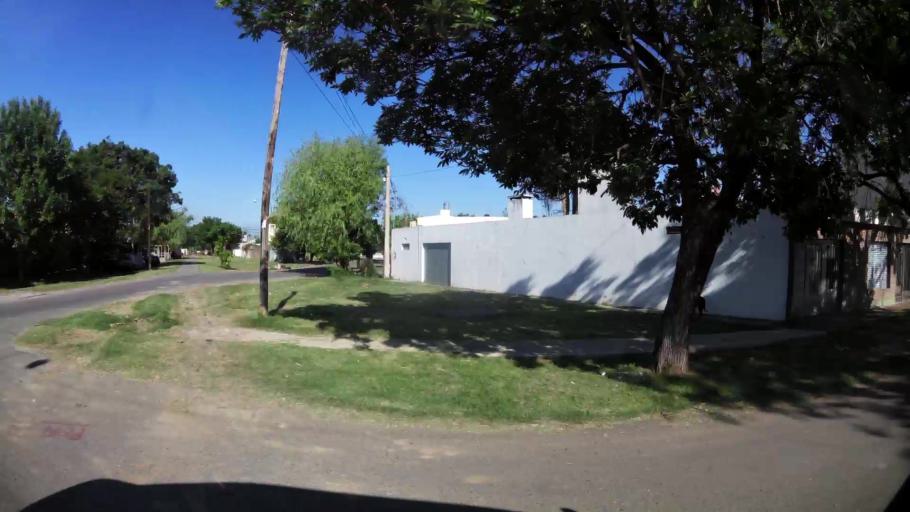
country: AR
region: Santa Fe
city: Santa Fe de la Vera Cruz
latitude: -31.6150
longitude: -60.6912
